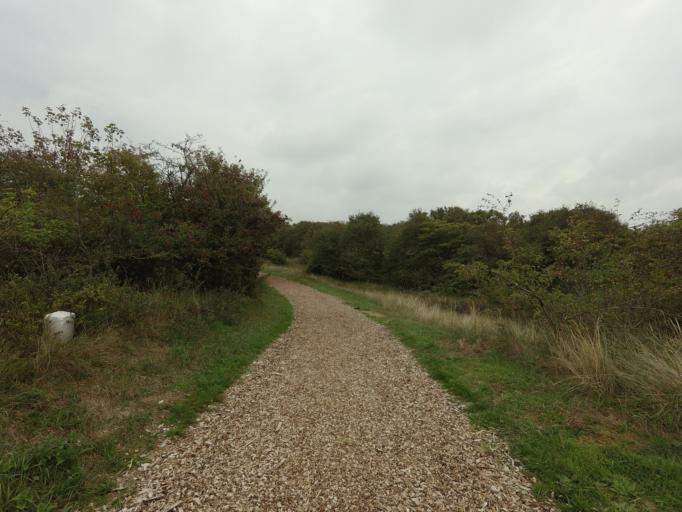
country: NL
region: Friesland
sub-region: Gemeente Schiermonnikoog
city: Schiermonnikoog
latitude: 53.4860
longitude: 6.1833
